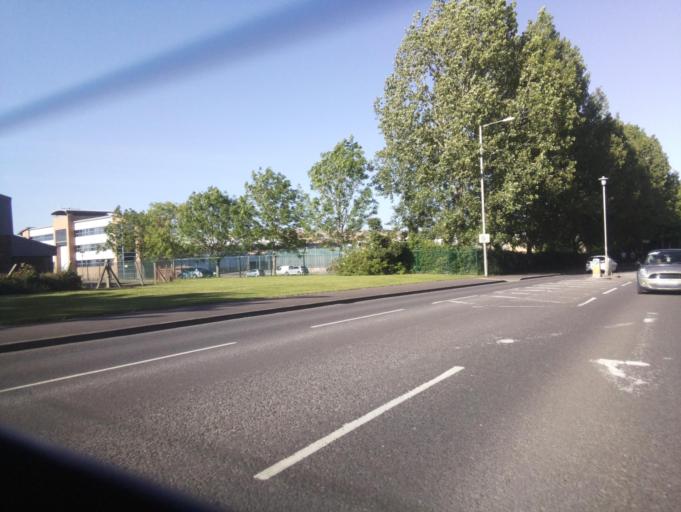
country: GB
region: England
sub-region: Somerset
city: Yeovil
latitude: 50.9337
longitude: -2.6560
